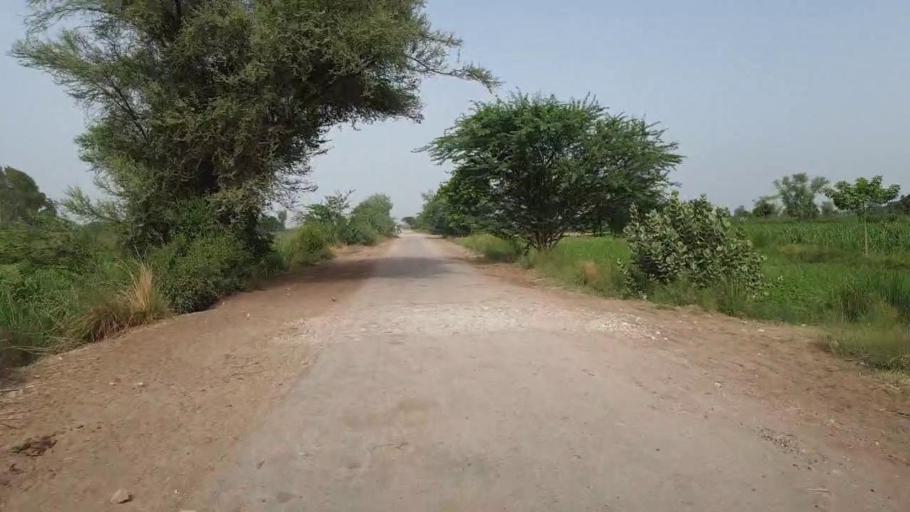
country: PK
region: Sindh
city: Daulatpur
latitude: 26.5461
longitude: 68.0708
